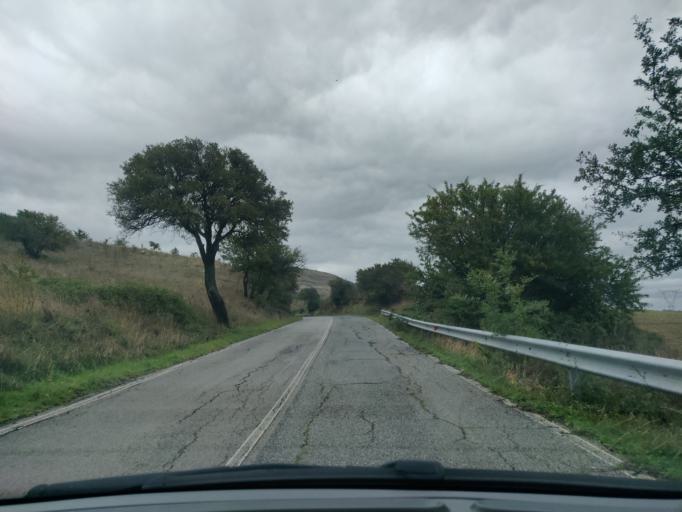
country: IT
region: Latium
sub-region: Citta metropolitana di Roma Capitale
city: Aurelia
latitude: 42.1309
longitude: 11.8430
